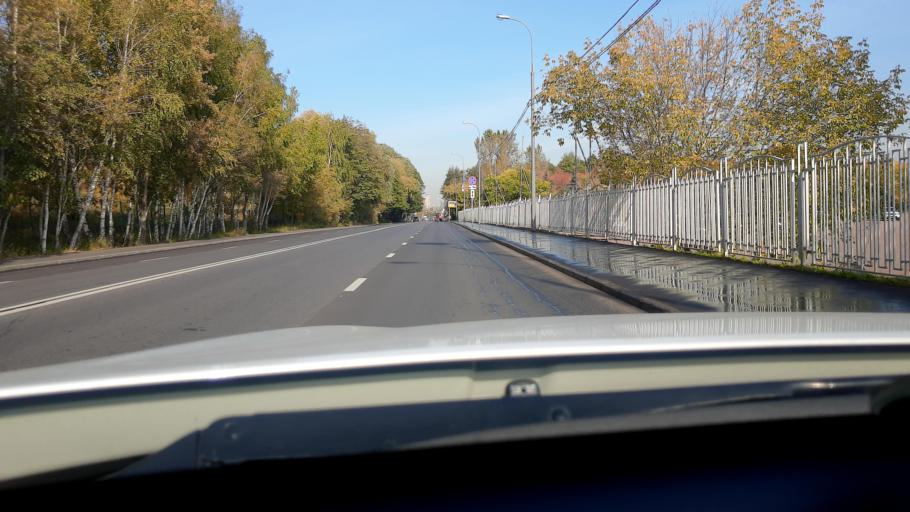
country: RU
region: Moscow
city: Shchukino
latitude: 55.7631
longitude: 37.4305
